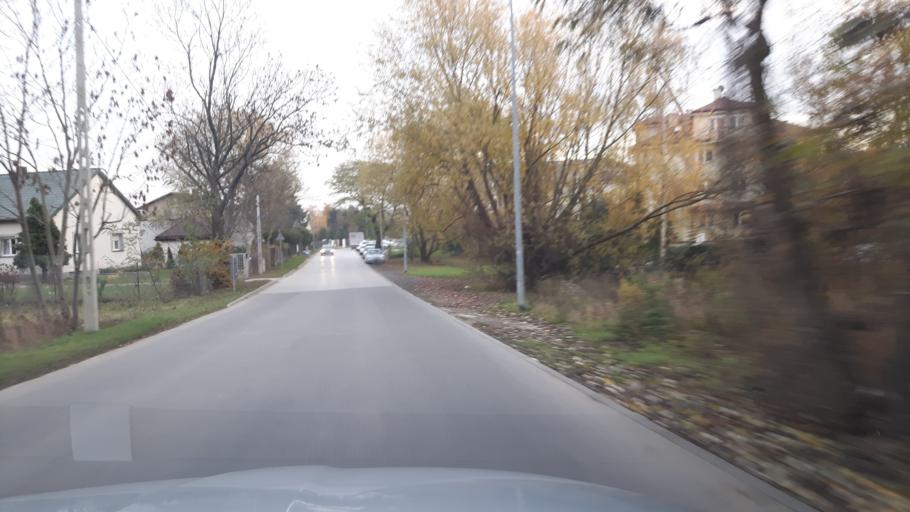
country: PL
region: Masovian Voivodeship
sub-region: Warszawa
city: Wilanow
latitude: 52.1814
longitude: 21.0990
